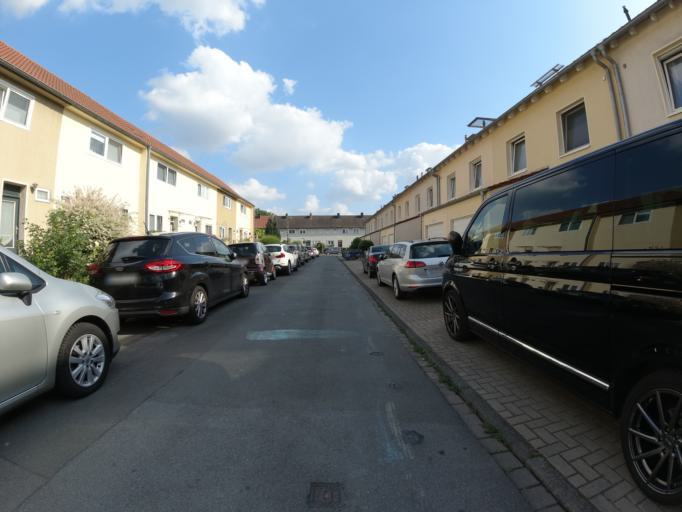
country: DE
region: North Rhine-Westphalia
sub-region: Regierungsbezirk Dusseldorf
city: Hochfeld
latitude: 51.3797
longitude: 6.6884
